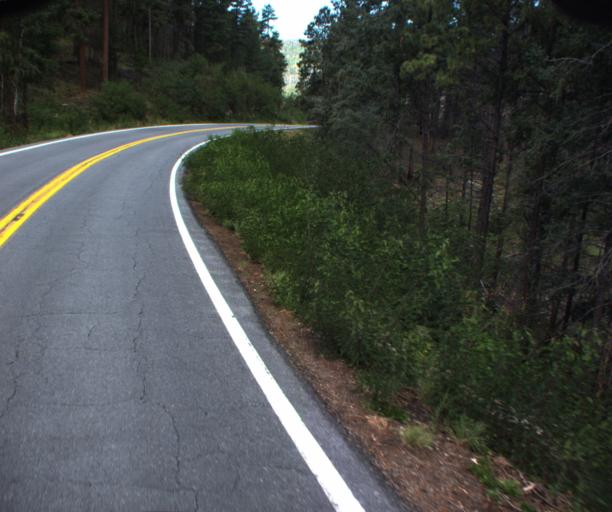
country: US
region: Arizona
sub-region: Apache County
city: Eagar
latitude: 33.7608
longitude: -109.2104
